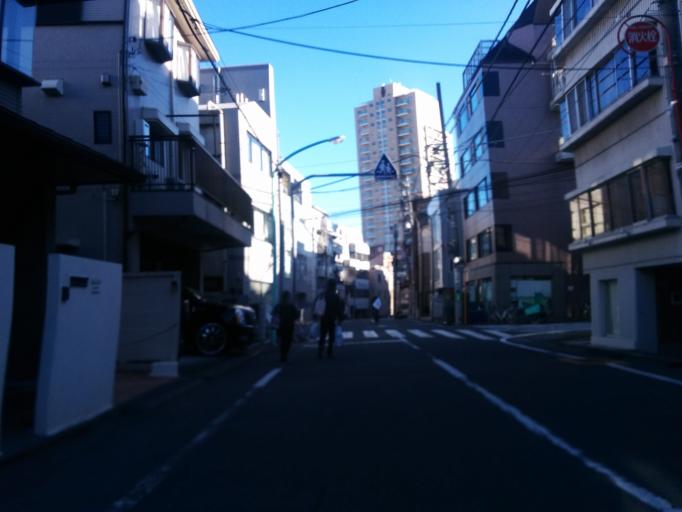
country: JP
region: Tokyo
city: Tokyo
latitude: 35.6761
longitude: 139.7080
